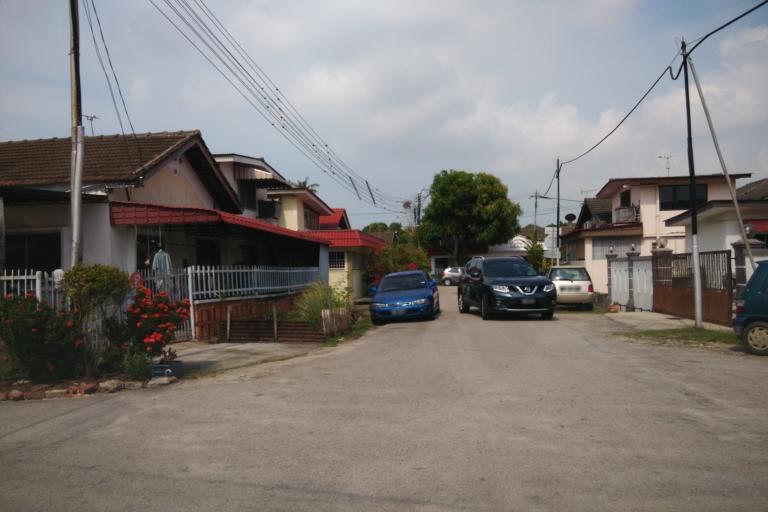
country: MY
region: Melaka
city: Malacca
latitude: 2.2096
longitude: 102.2423
